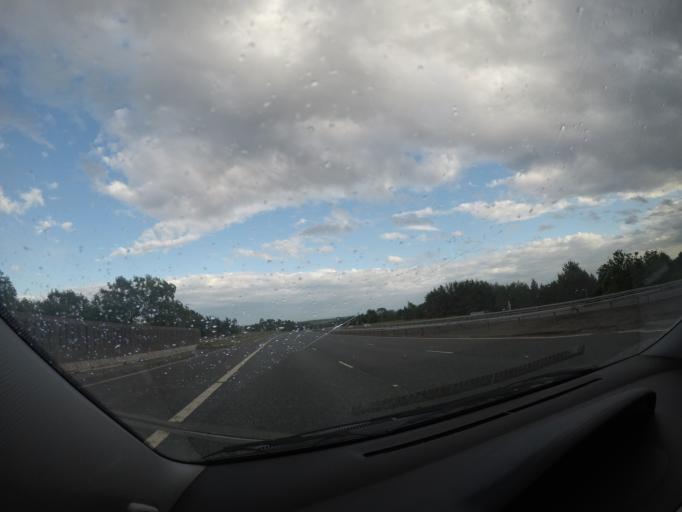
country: GB
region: Scotland
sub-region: Dumfries and Galloway
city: Gretna
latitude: 55.0015
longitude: -3.0598
